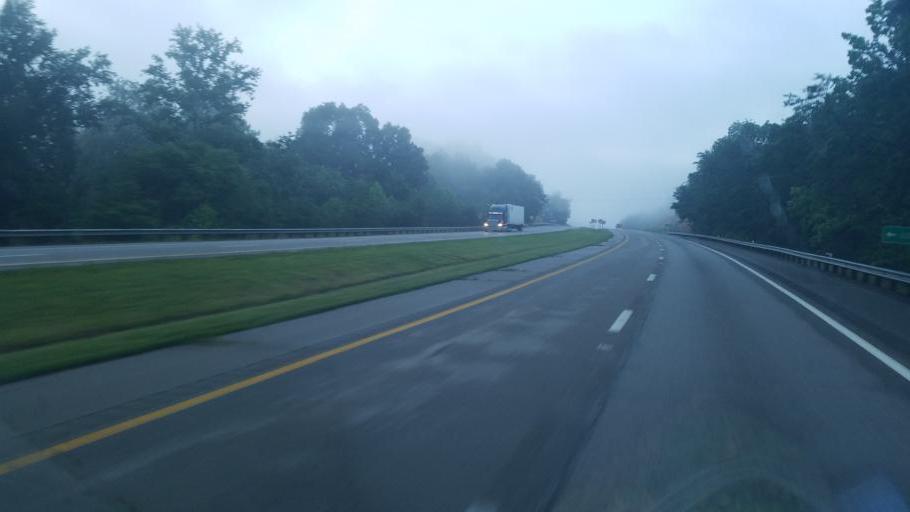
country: US
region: Ohio
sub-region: Jackson County
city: Jackson
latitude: 39.1111
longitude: -82.6795
